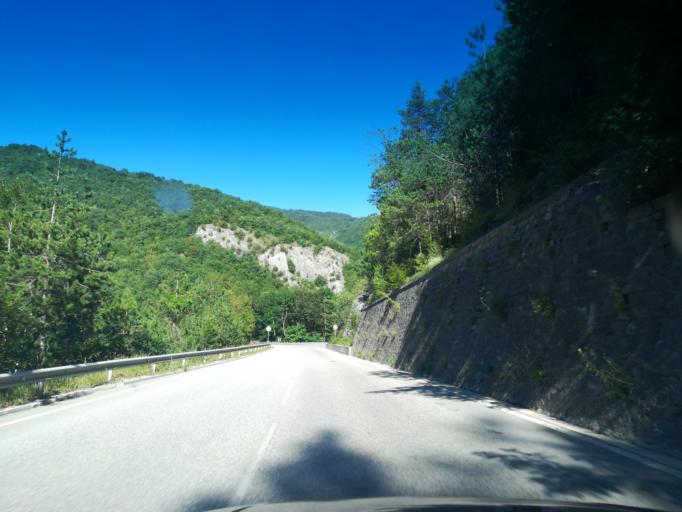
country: BG
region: Smolyan
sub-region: Obshtina Chepelare
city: Chepelare
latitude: 41.8216
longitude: 24.6932
